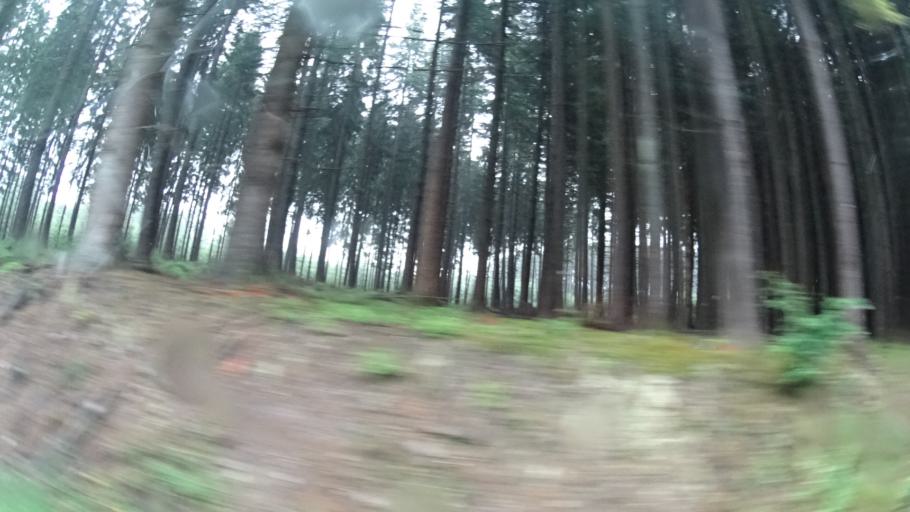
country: BE
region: Wallonia
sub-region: Province de Namur
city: Bievre
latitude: 49.9688
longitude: 5.0131
